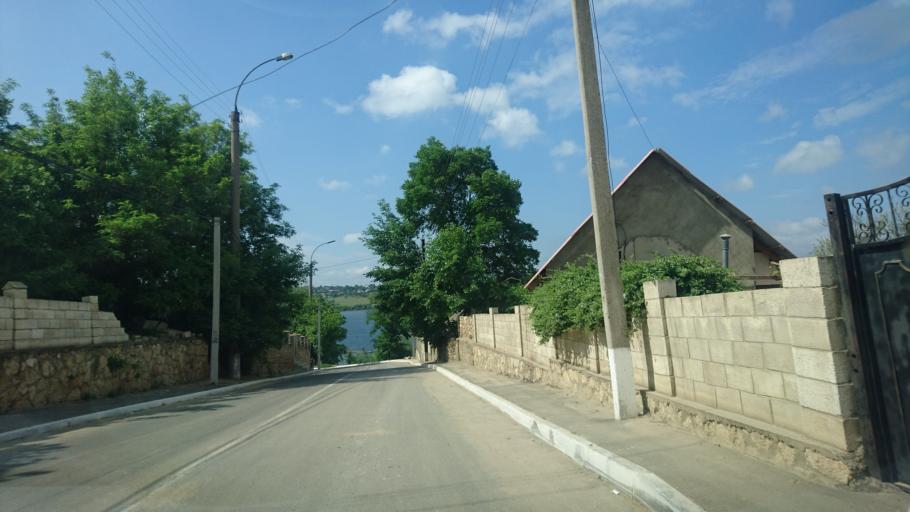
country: MD
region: Telenesti
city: Cocieri
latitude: 47.3553
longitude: 29.1064
